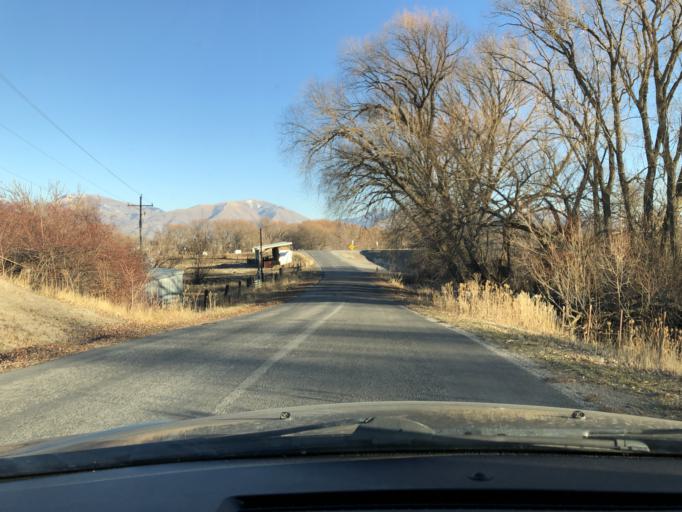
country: US
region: Utah
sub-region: Cache County
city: Wellsville
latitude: 41.6465
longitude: -111.9262
